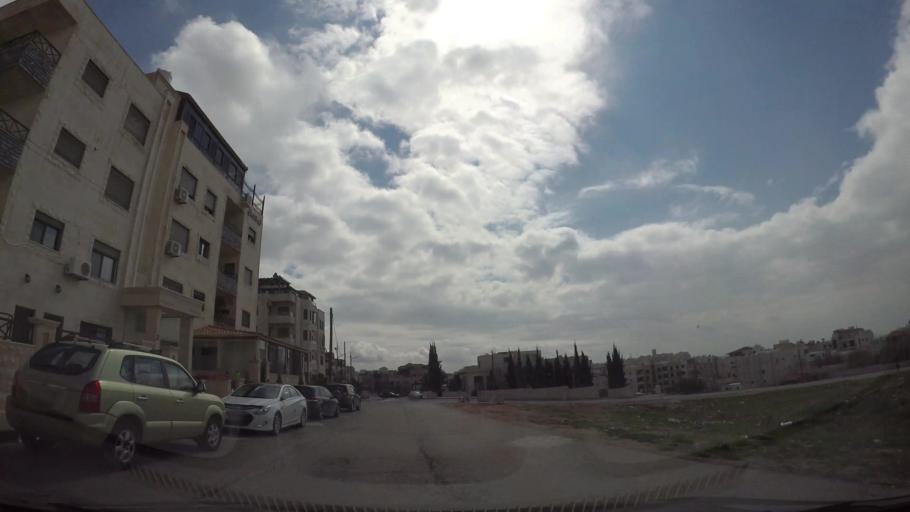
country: JO
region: Amman
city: Wadi as Sir
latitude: 31.9628
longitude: 35.8367
